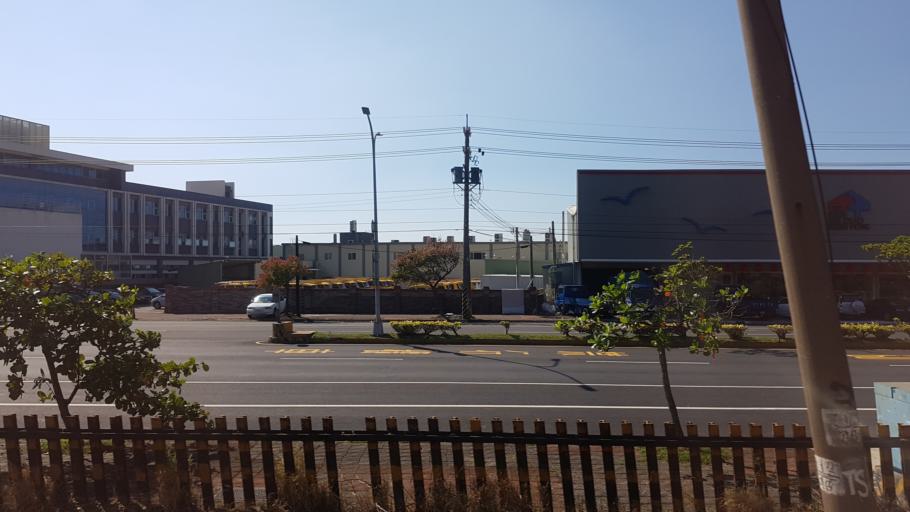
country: TW
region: Taiwan
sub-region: Hsinchu
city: Hsinchu
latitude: 24.7797
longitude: 120.9192
